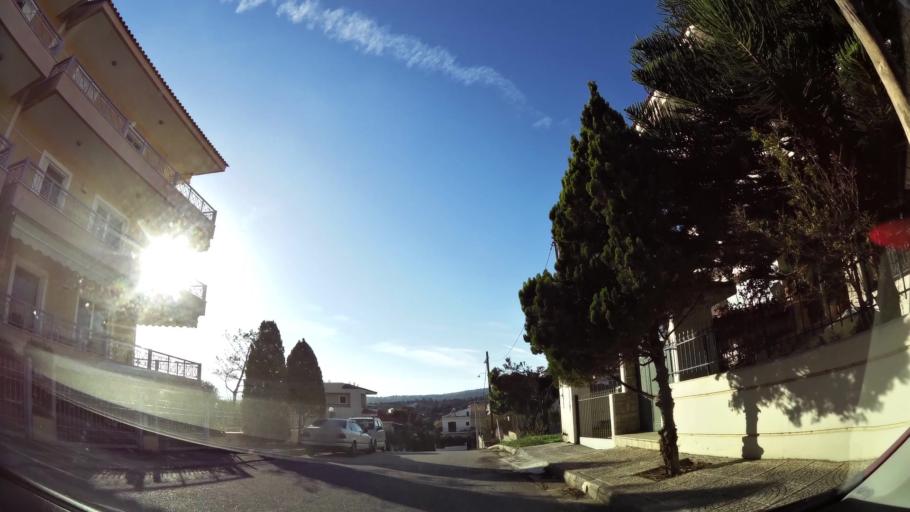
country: GR
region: Attica
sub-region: Nomarchia Anatolikis Attikis
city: Rafina
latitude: 38.0244
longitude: 23.9996
